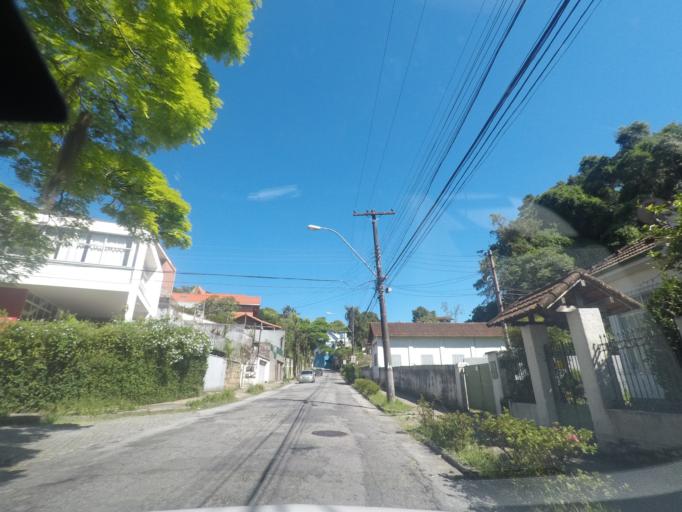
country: BR
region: Rio de Janeiro
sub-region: Petropolis
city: Petropolis
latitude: -22.5143
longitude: -43.1882
